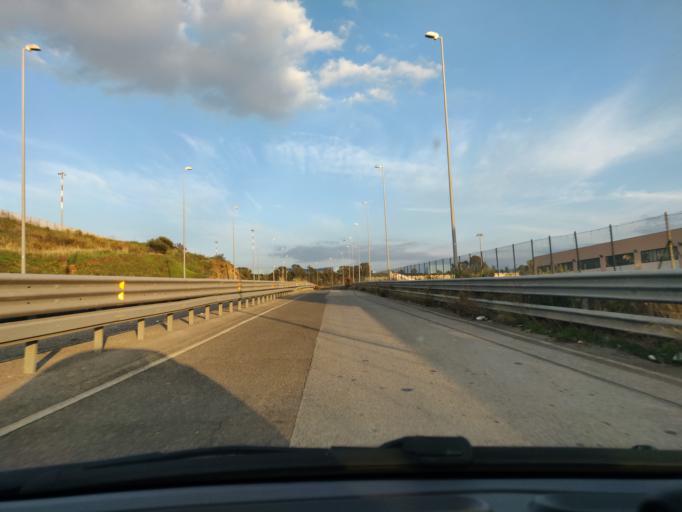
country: IT
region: Latium
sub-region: Citta metropolitana di Roma Capitale
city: Aurelia
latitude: 42.1246
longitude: 11.7808
